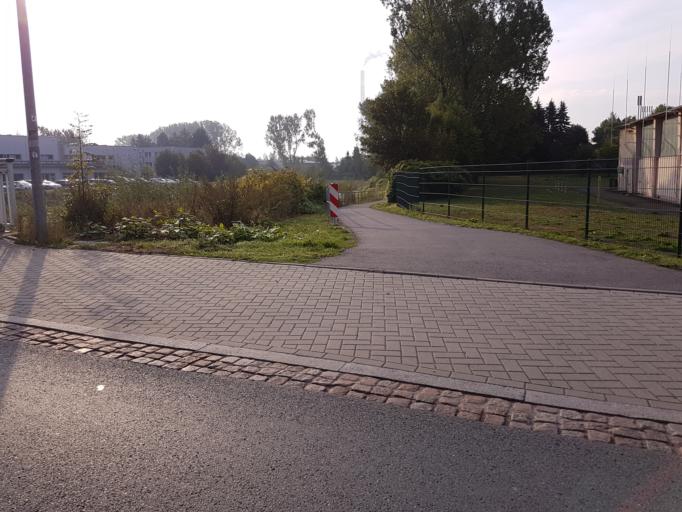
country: DE
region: Saxony
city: Wittgensdorf
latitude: 50.8673
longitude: 12.9051
